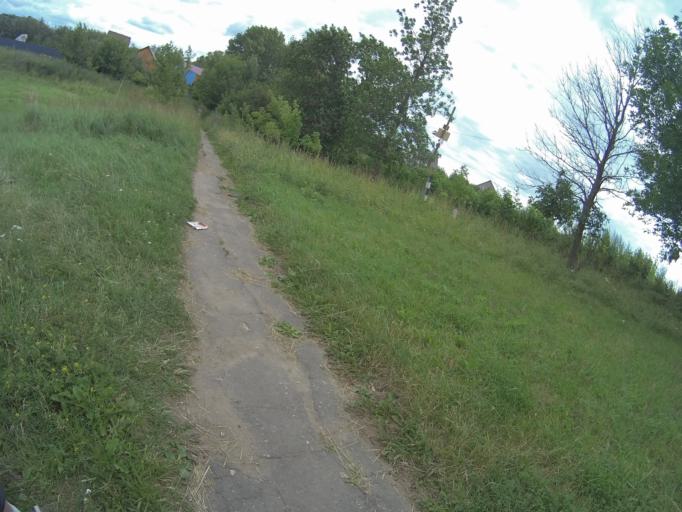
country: RU
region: Vladimir
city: Bogolyubovo
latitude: 56.2077
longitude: 40.5280
